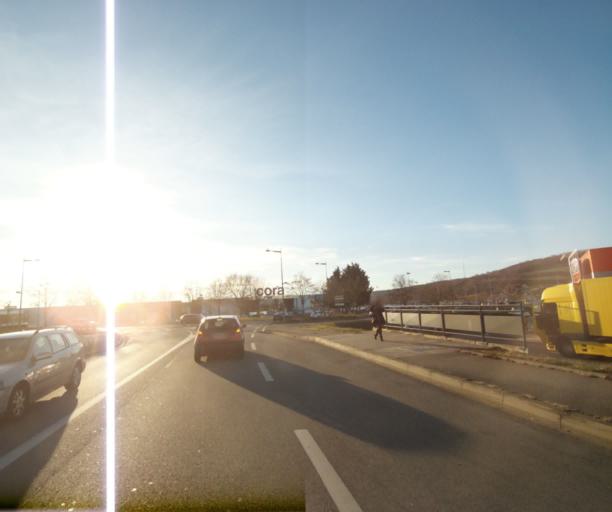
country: FR
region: Lorraine
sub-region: Departement de Meurthe-et-Moselle
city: Pulnoy
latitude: 48.7045
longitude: 6.2469
